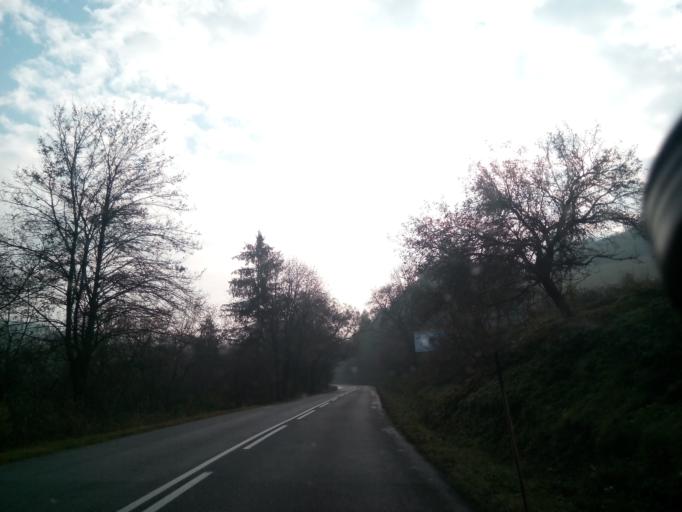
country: SK
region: Kosicky
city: Gelnica
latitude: 48.8720
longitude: 21.0019
